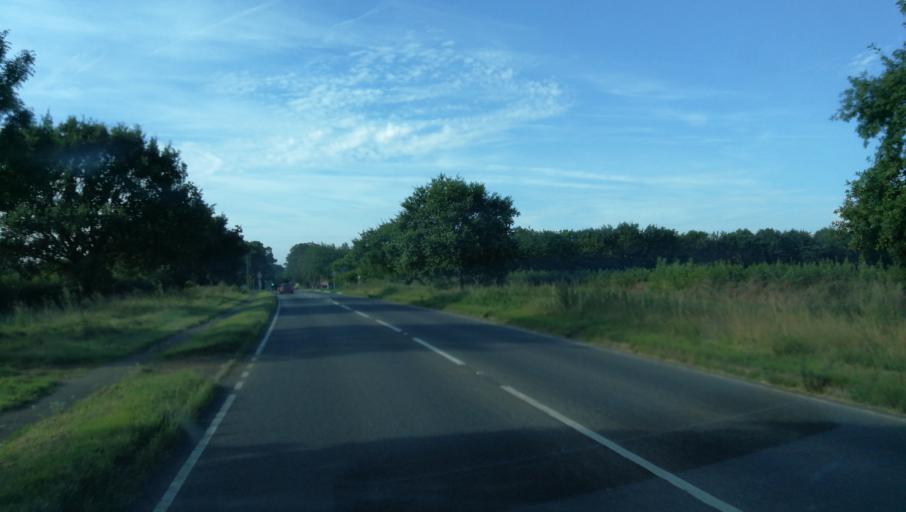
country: GB
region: England
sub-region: Oxfordshire
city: Deddington
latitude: 51.9862
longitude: -1.3223
